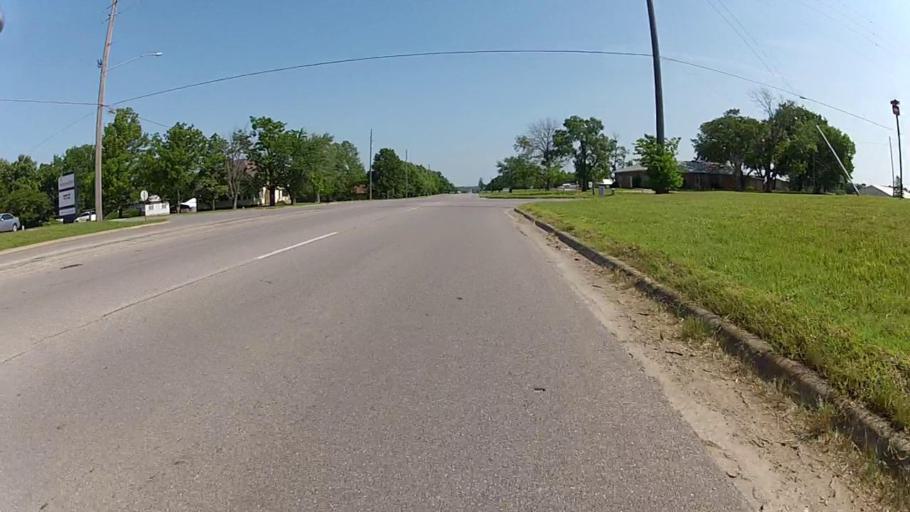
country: US
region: Kansas
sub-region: Montgomery County
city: Independence
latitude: 37.1960
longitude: -95.7106
